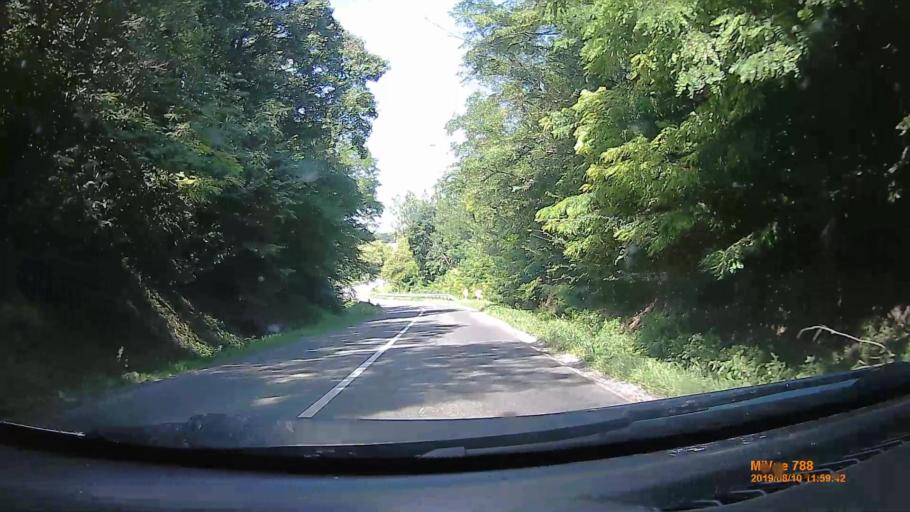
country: HU
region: Somogy
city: Somogyvar
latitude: 46.5438
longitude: 17.6521
